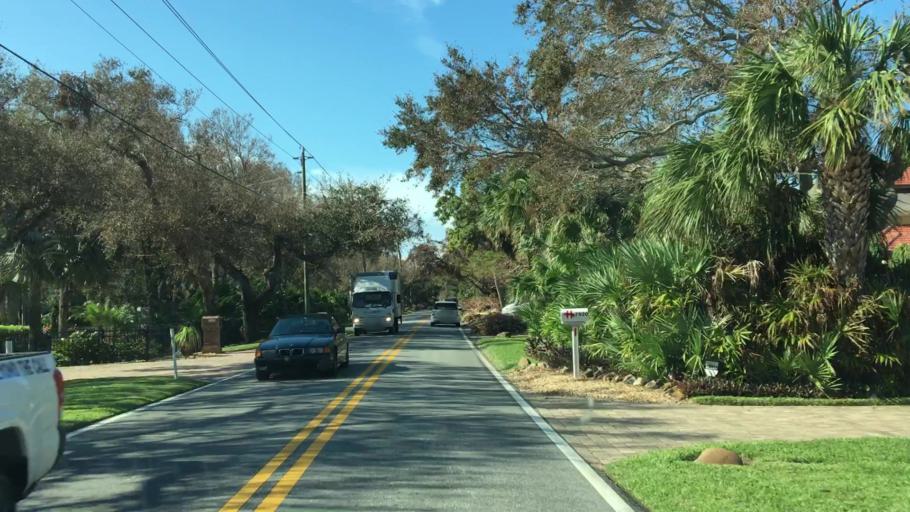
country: US
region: Florida
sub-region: Brevard County
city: South Patrick Shores
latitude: 28.2151
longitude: -80.6421
